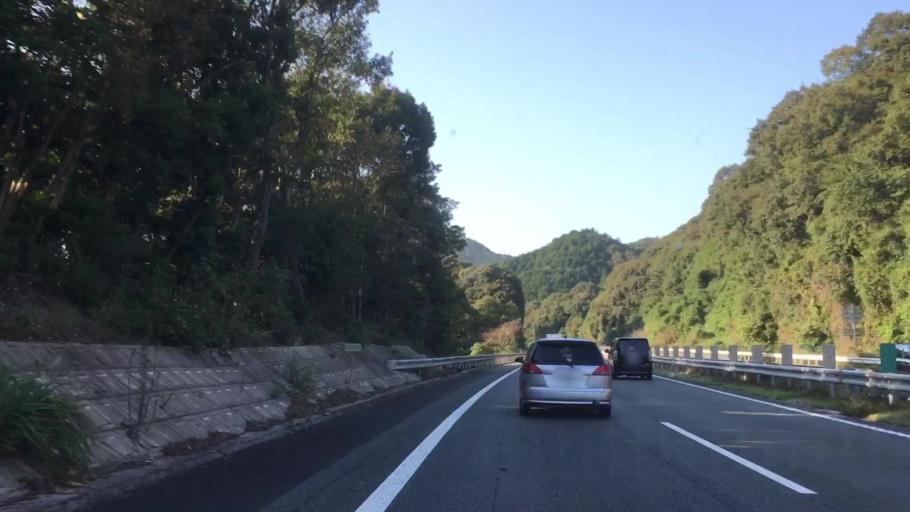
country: JP
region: Yamaguchi
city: Ogori-shimogo
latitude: 34.1315
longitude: 131.3767
